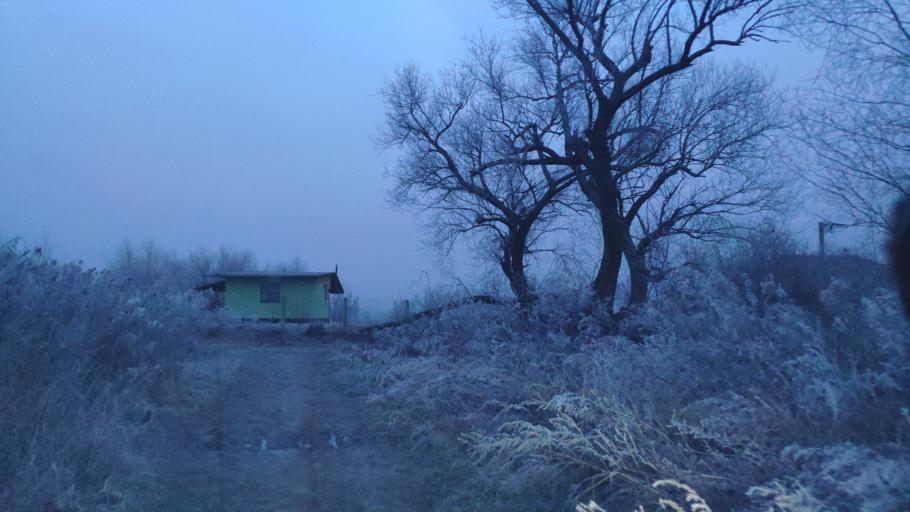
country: SK
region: Kosicky
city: Kosice
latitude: 48.6128
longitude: 21.3354
